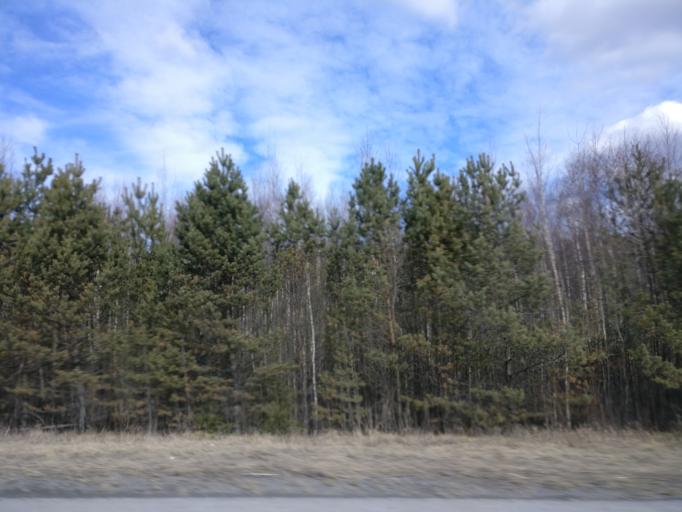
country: FI
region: Haeme
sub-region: Haemeenlinna
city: Parola
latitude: 61.0664
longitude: 24.3176
